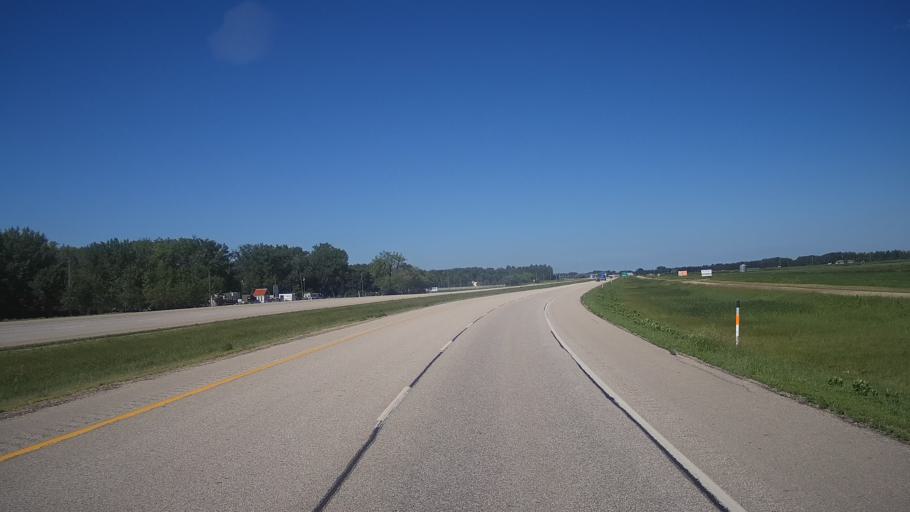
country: CA
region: Manitoba
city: Portage la Prairie
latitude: 49.9608
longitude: -98.2428
